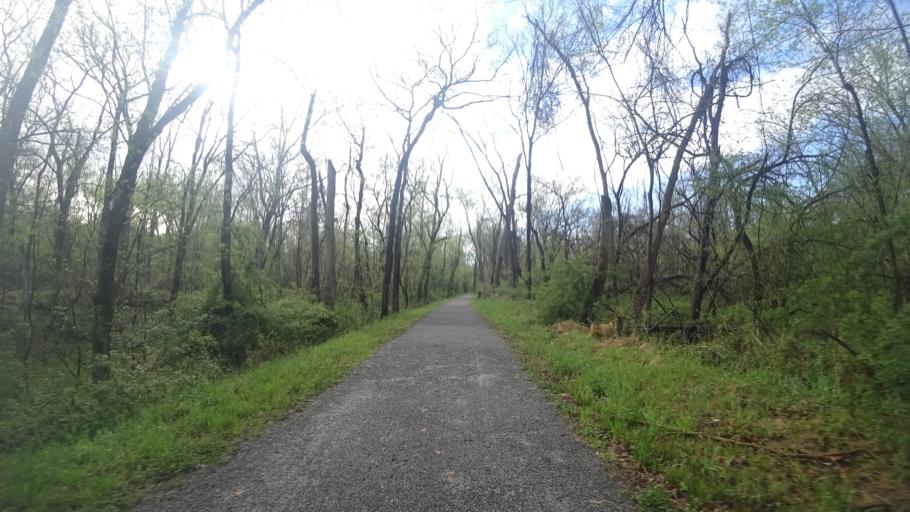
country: US
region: Virginia
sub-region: Loudoun County
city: Belmont
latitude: 39.1095
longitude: -77.4760
